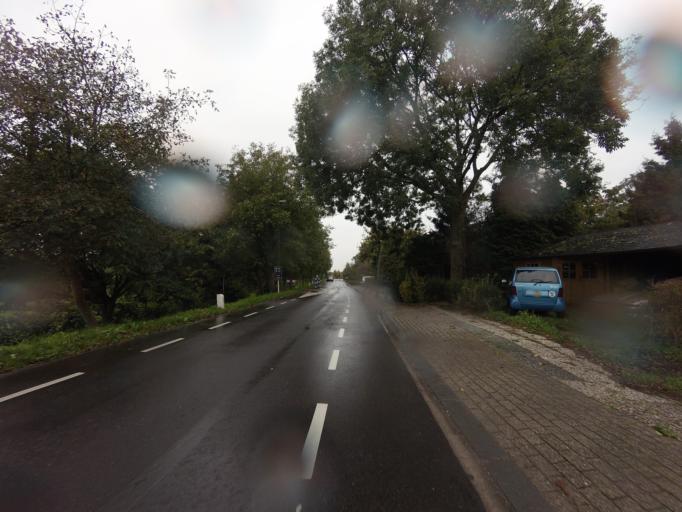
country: NL
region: South Holland
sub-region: Molenwaard
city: Liesveld
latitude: 51.9269
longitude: 4.8248
